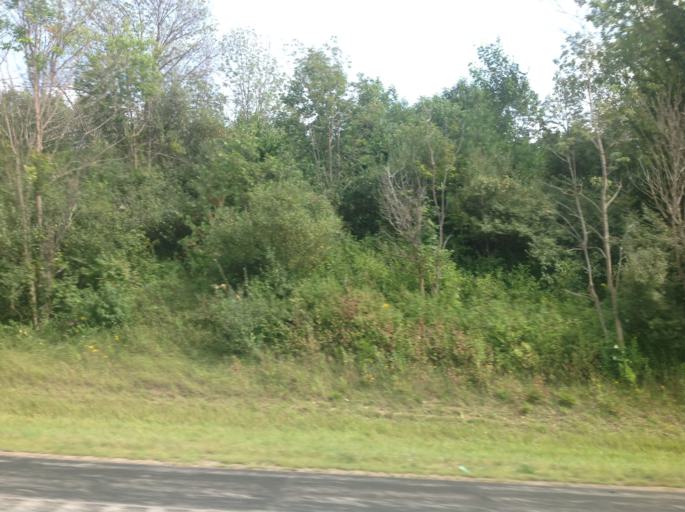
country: US
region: Ohio
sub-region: Richland County
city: Lincoln Heights
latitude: 40.7259
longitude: -82.4763
